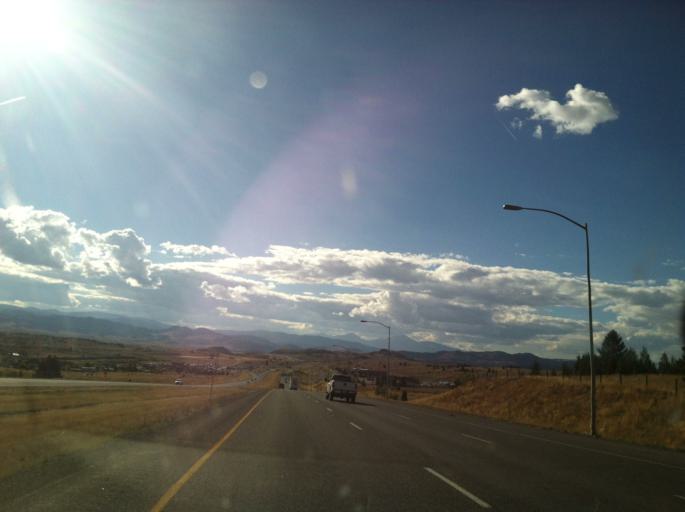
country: US
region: Montana
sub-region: Silver Bow County
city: Butte
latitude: 46.0063
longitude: -112.5977
